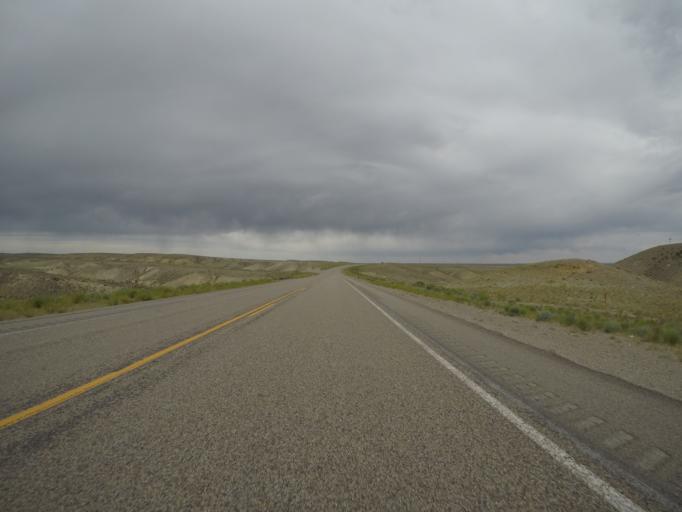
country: US
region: Wyoming
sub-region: Lincoln County
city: Kemmerer
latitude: 41.9718
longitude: -110.0606
